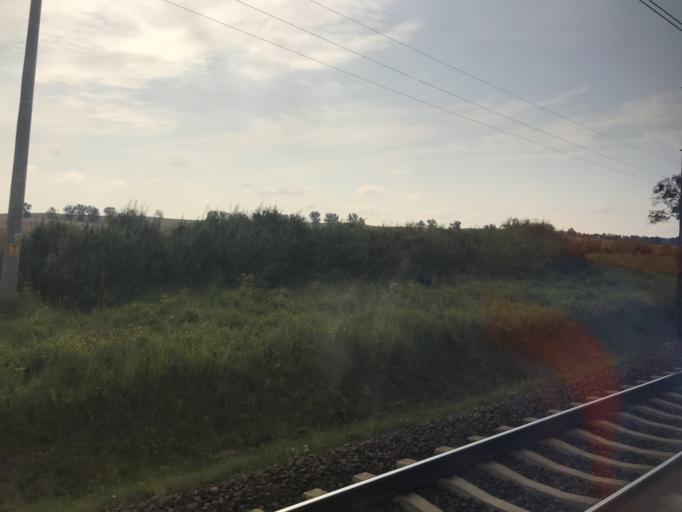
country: PL
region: Pomeranian Voivodeship
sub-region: Powiat starogardzki
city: Smetowo Graniczne
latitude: 53.8101
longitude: 18.6761
